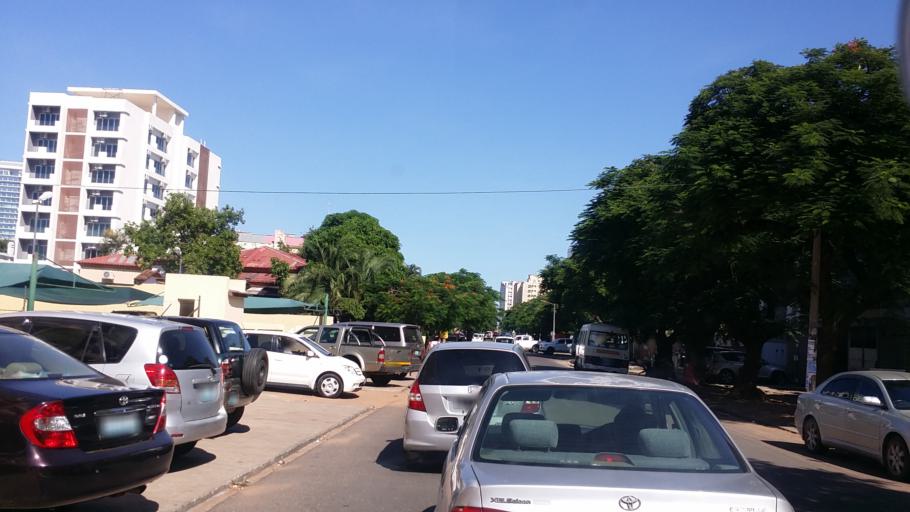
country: MZ
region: Maputo City
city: Maputo
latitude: -25.9727
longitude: 32.5884
